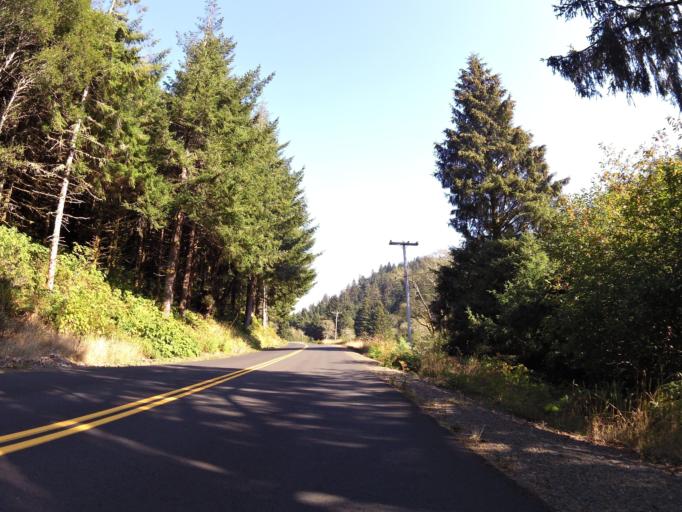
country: US
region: Oregon
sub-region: Lincoln County
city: Rose Lodge
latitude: 45.0861
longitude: -123.9608
